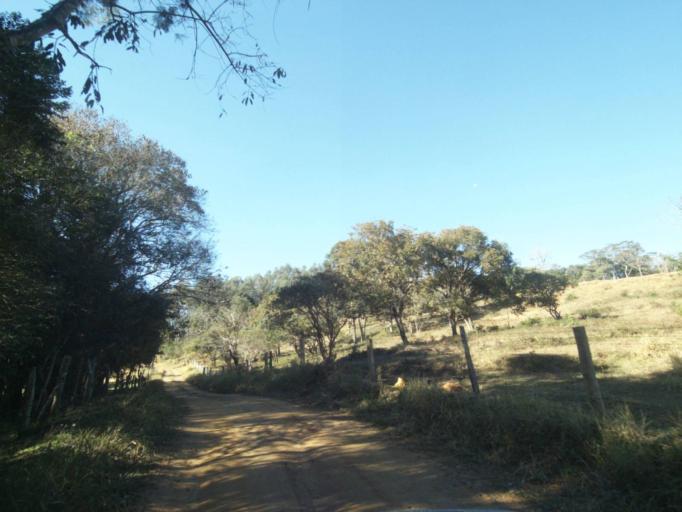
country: BR
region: Parana
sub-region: Tibagi
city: Tibagi
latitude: -24.5565
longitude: -50.5192
